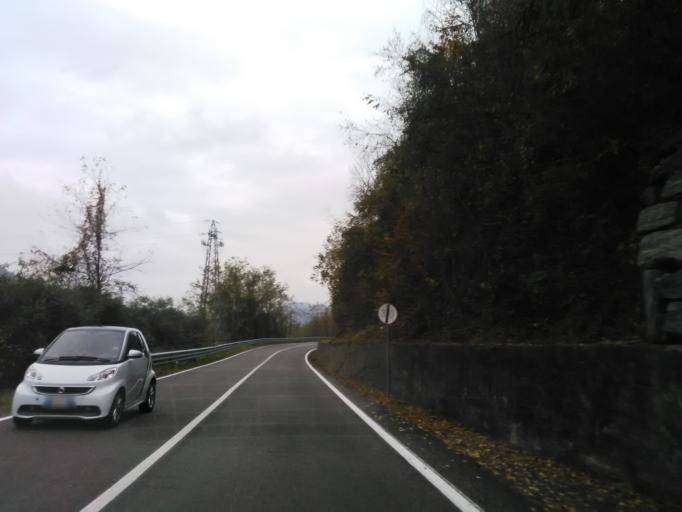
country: IT
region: Piedmont
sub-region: Provincia di Vercelli
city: Varallo
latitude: 45.7929
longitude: 8.2676
